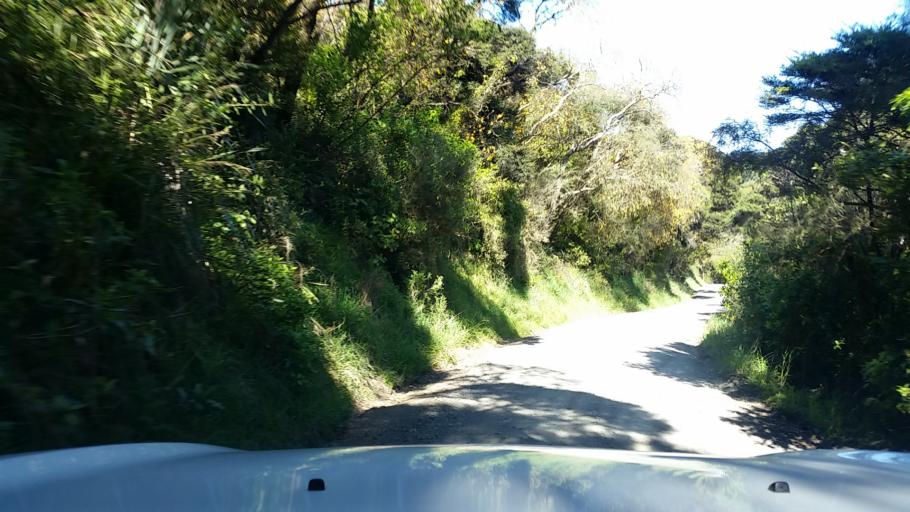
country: NZ
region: Auckland
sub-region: Auckland
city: Titirangi
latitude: -37.0371
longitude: 174.5138
